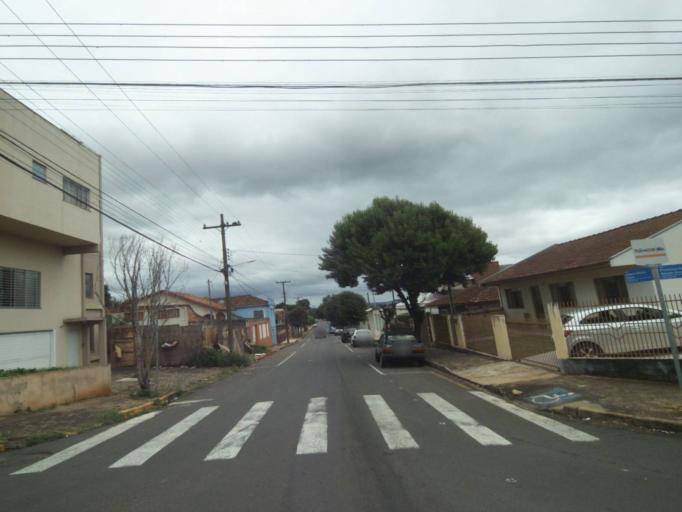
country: BR
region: Parana
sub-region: Telemaco Borba
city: Telemaco Borba
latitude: -24.3283
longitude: -50.6154
